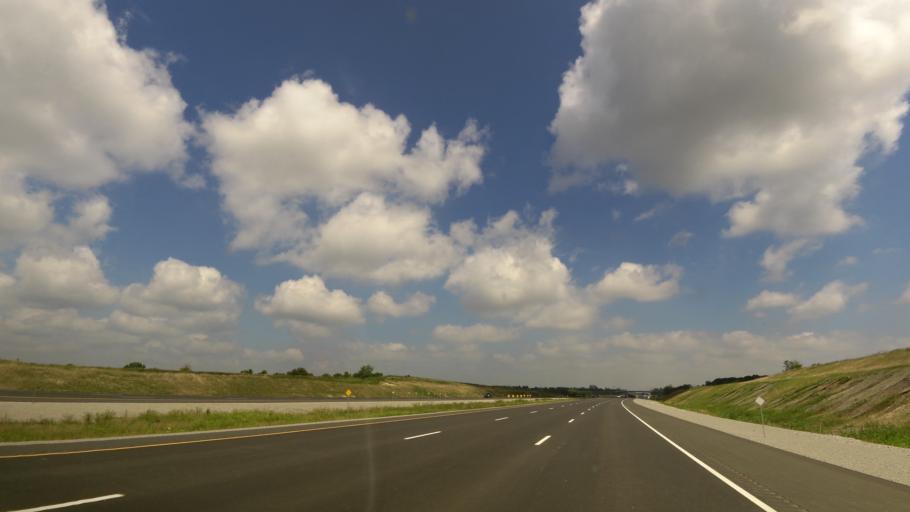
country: CA
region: Ontario
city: Pickering
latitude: 43.9383
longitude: -79.0682
